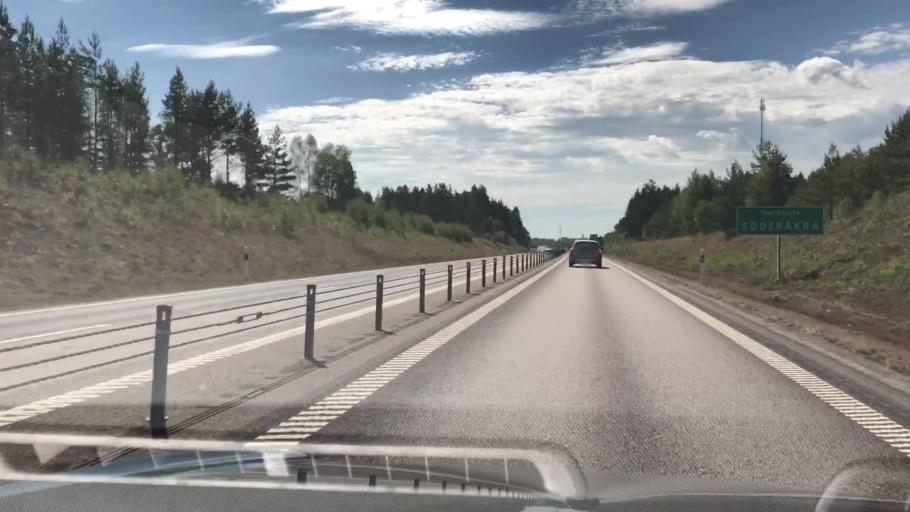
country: SE
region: Kalmar
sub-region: Torsas Kommun
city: Torsas
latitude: 56.4631
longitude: 16.0784
